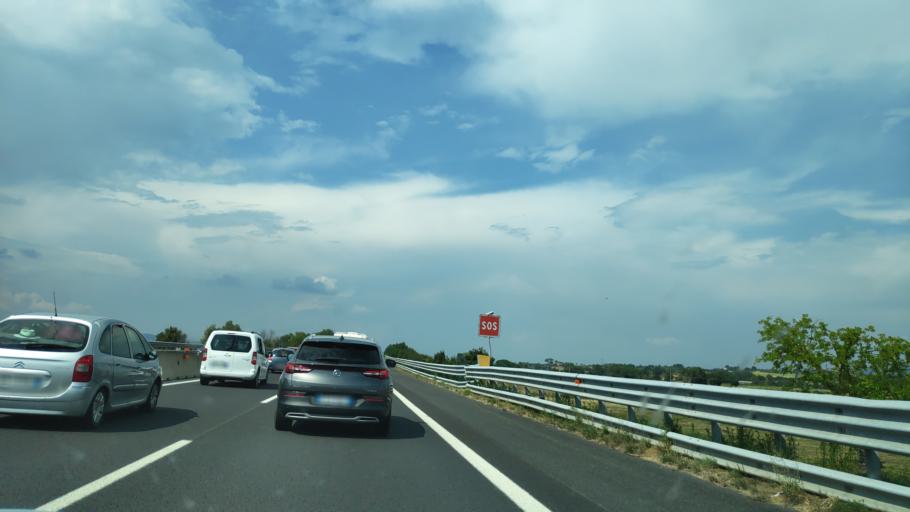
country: IT
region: Tuscany
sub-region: Province of Arezzo
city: Lucignano
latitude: 43.2901
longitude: 11.7640
